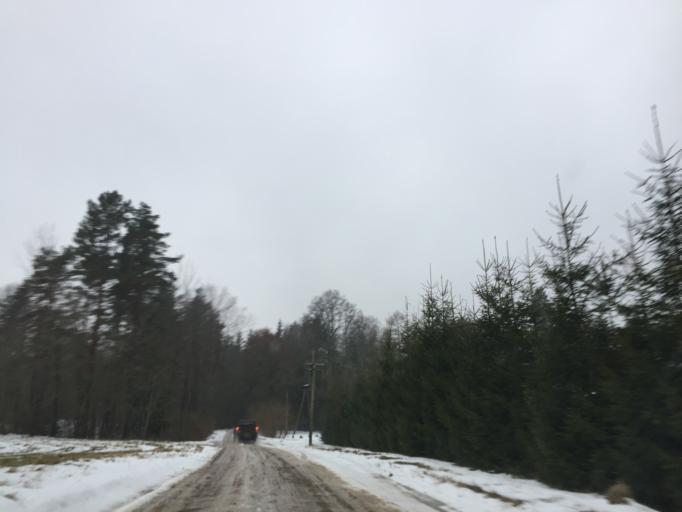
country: LV
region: Incukalns
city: Vangazi
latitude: 57.1267
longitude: 24.5722
